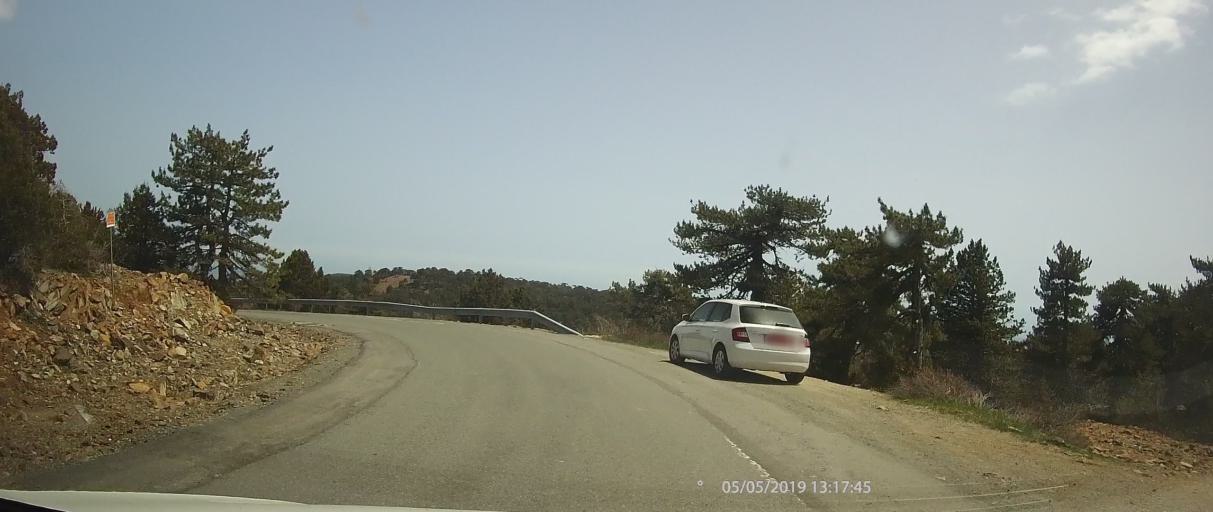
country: CY
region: Lefkosia
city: Kakopetria
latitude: 34.9354
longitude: 32.8623
